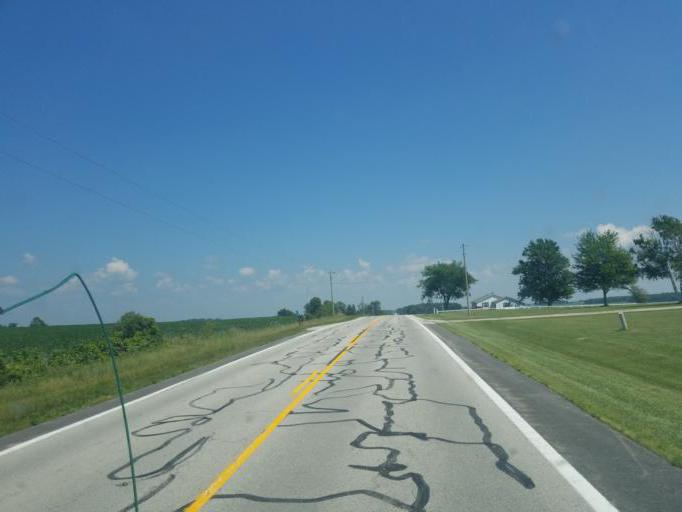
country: US
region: Ohio
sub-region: Shelby County
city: Jackson Center
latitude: 40.3958
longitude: -84.0900
